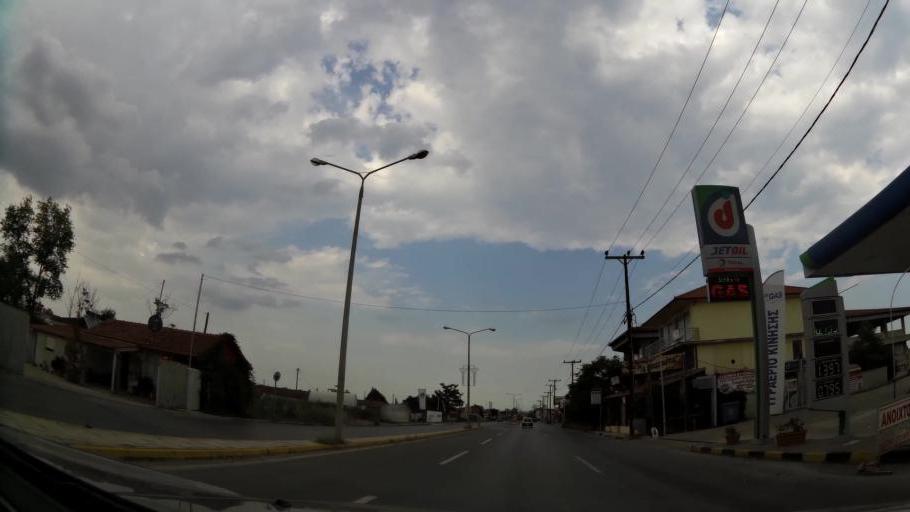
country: GR
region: Central Macedonia
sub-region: Nomos Imathias
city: Veroia
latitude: 40.5342
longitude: 22.2090
